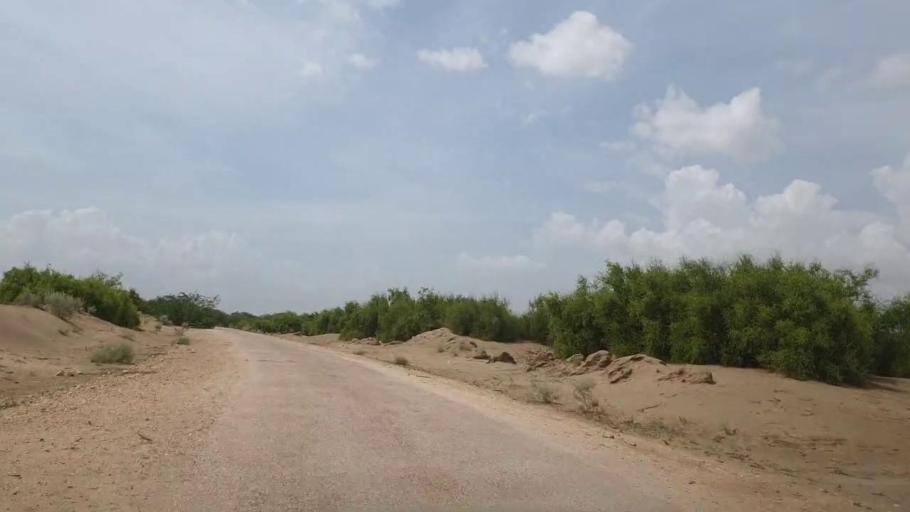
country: PK
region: Sindh
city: Kot Diji
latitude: 27.2332
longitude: 69.0886
